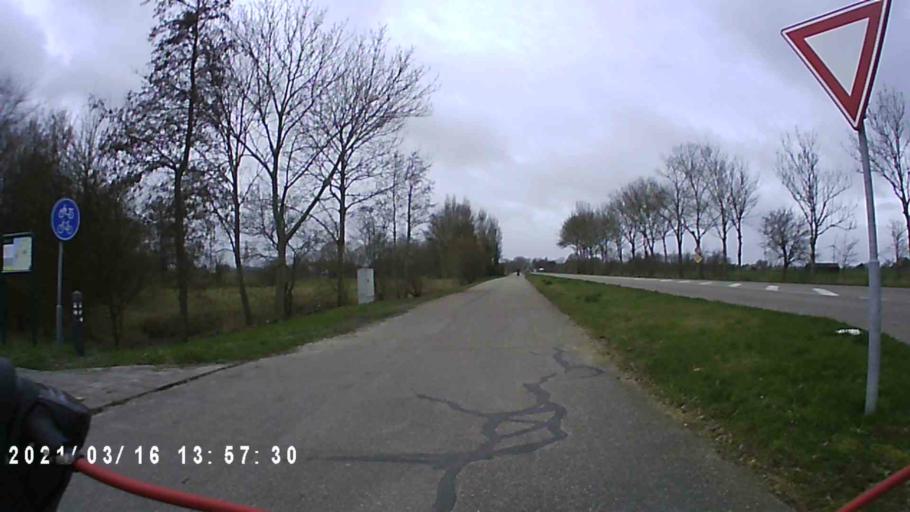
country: NL
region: Friesland
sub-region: Gemeente Franekeradeel
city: Franeker
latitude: 53.1838
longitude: 5.5069
